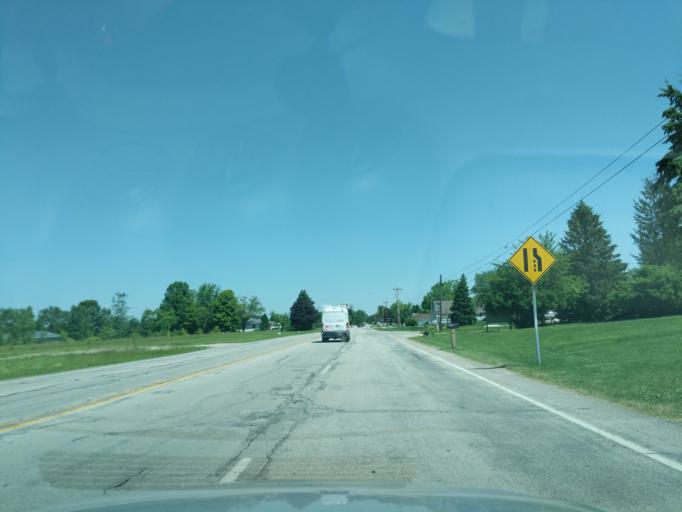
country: US
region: Indiana
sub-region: Whitley County
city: Columbia City
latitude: 41.1708
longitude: -85.4915
